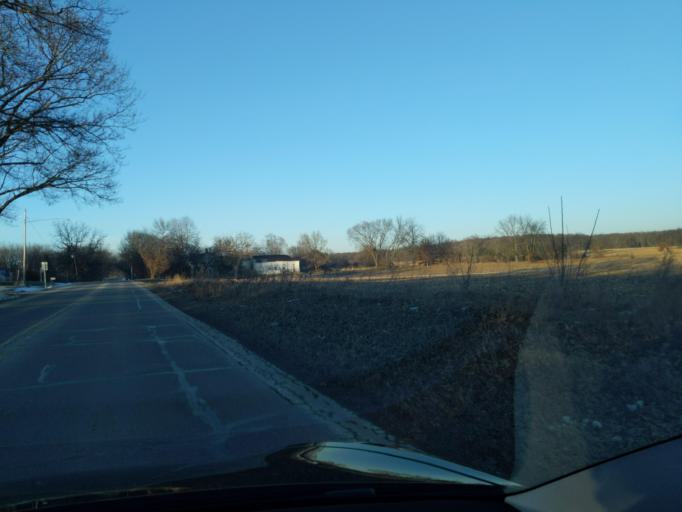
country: US
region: Michigan
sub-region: Ingham County
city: Stockbridge
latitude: 42.4666
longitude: -84.0848
